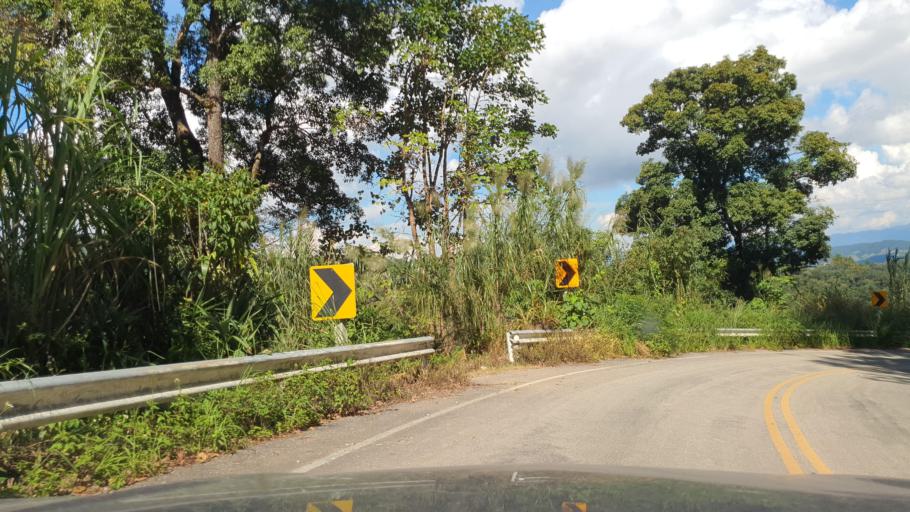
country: TH
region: Chiang Mai
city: Phrao
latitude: 19.3092
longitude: 99.3409
